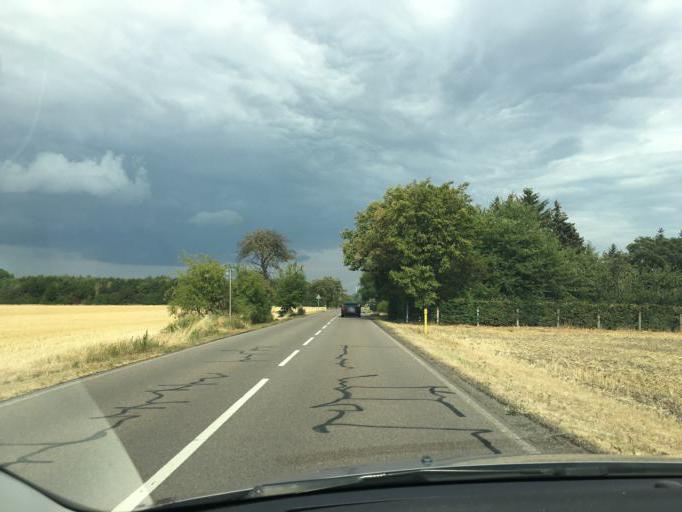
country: DE
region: Saxony
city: Rackwitz
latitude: 51.3940
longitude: 12.3523
